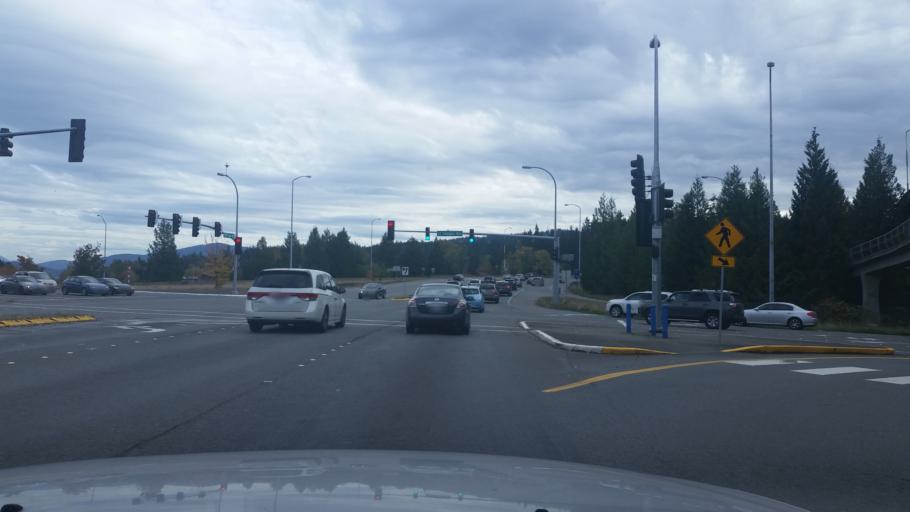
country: US
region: Washington
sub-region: King County
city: Eastgate
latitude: 47.5810
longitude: -122.1418
